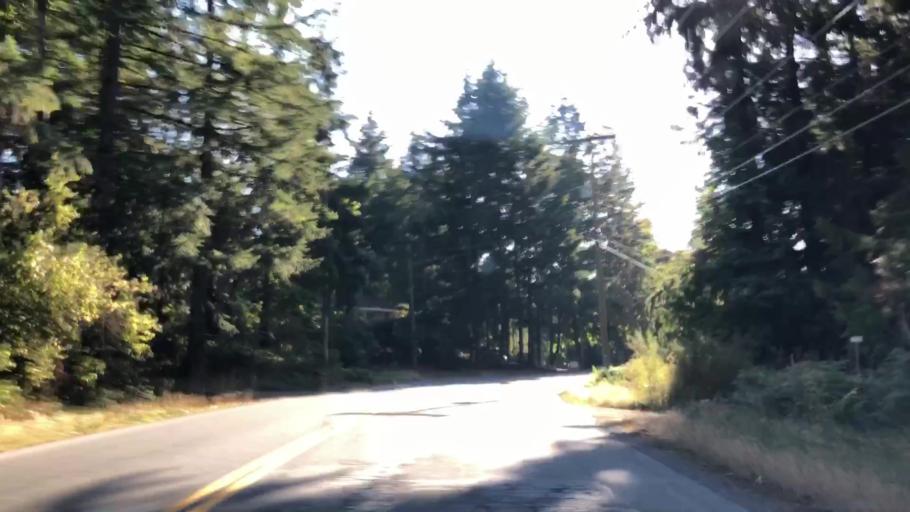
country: CA
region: British Columbia
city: North Saanich
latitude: 48.6868
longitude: -123.5713
